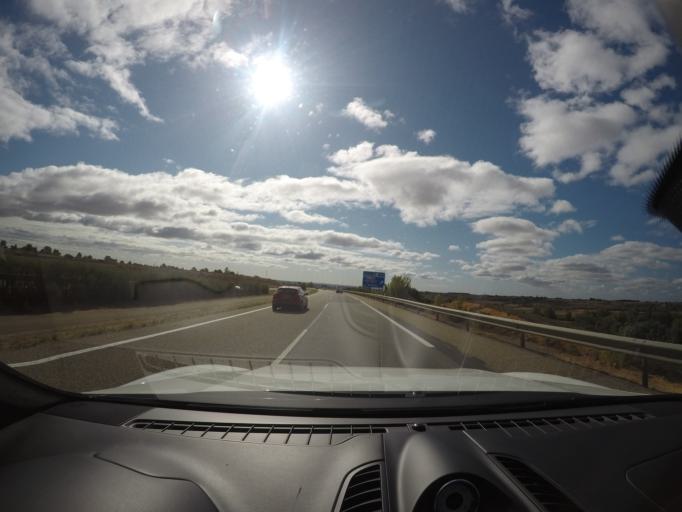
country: ES
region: Castille and Leon
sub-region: Provincia de Leon
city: Onzonilla
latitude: 42.5421
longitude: -5.6151
